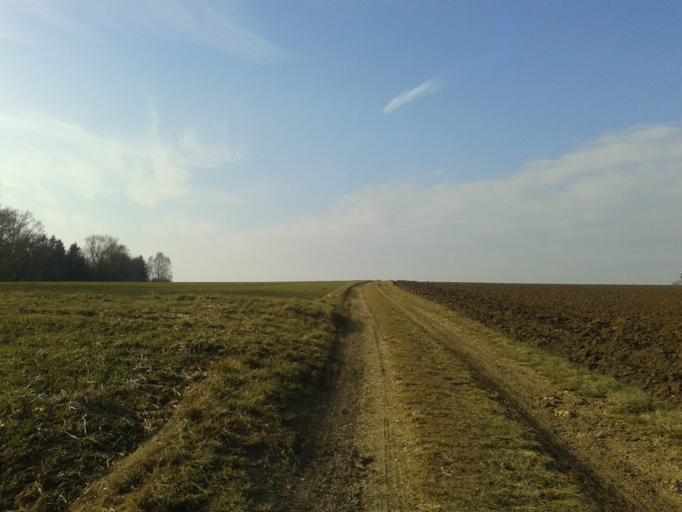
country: DE
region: Baden-Wuerttemberg
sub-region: Tuebingen Region
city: Oberdischingen
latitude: 48.3095
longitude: 9.8482
